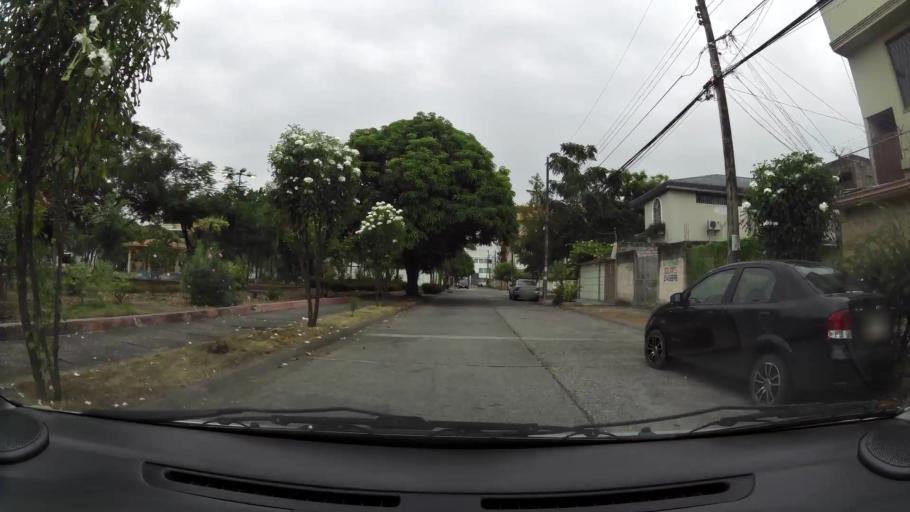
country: EC
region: Guayas
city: Eloy Alfaro
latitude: -2.1494
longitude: -79.8881
